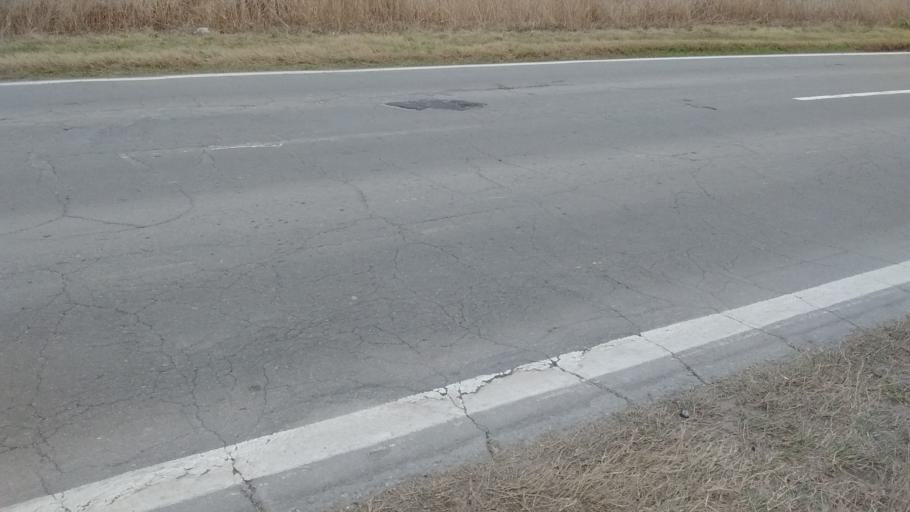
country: AR
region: Santa Fe
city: Las Rosas
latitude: -32.5802
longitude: -61.5483
